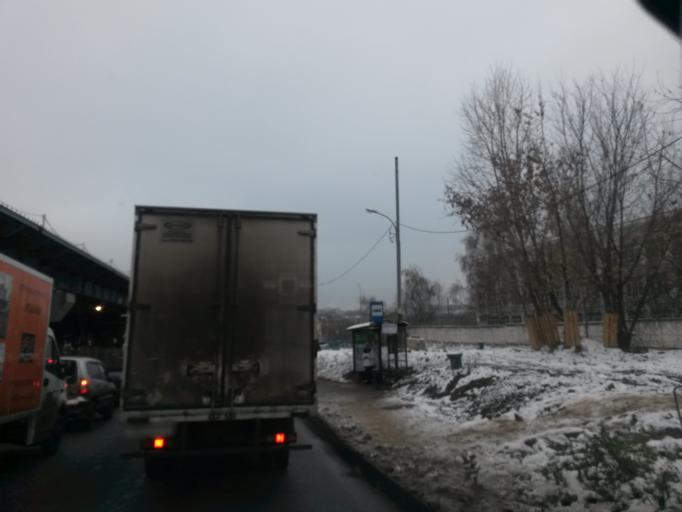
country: RU
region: Moscow
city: Mikhalkovo
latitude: 55.6883
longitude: 37.4279
